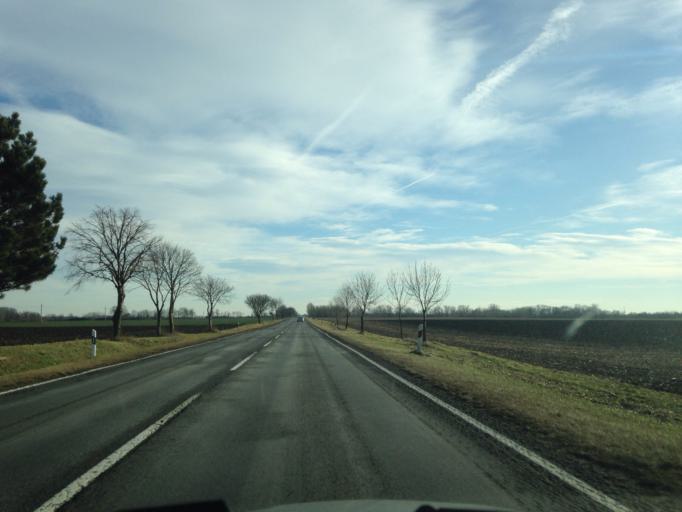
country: HU
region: Gyor-Moson-Sopron
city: Kimle
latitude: 47.7908
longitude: 17.4009
